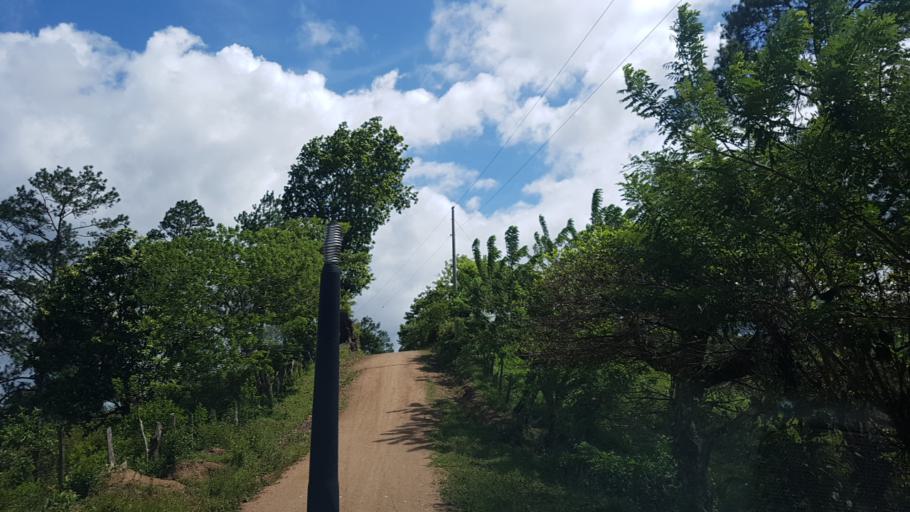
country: NI
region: Nueva Segovia
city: Ciudad Antigua
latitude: 13.6525
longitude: -86.2434
